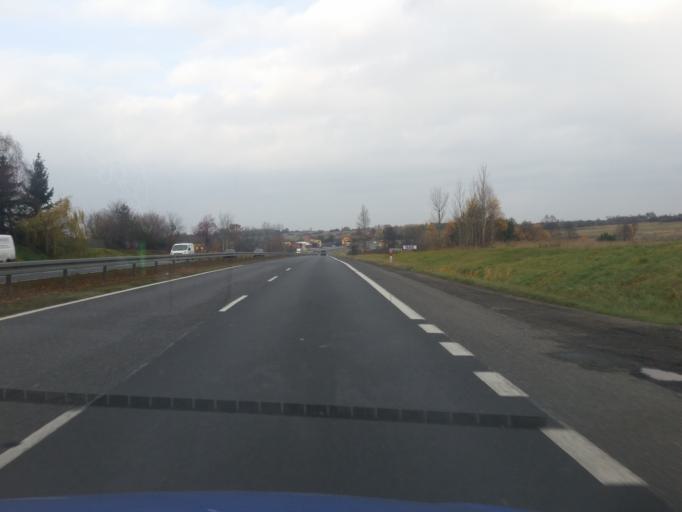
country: PL
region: Silesian Voivodeship
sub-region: Powiat myszkowski
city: Kozieglowy
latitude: 50.5719
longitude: 19.1655
